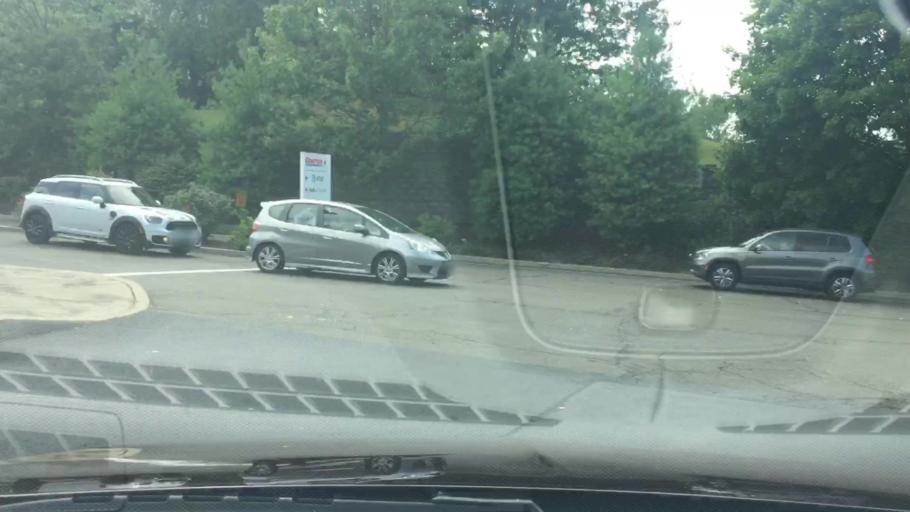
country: US
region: Connecticut
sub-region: Fairfield County
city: Darien
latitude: 41.0925
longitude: -73.4520
